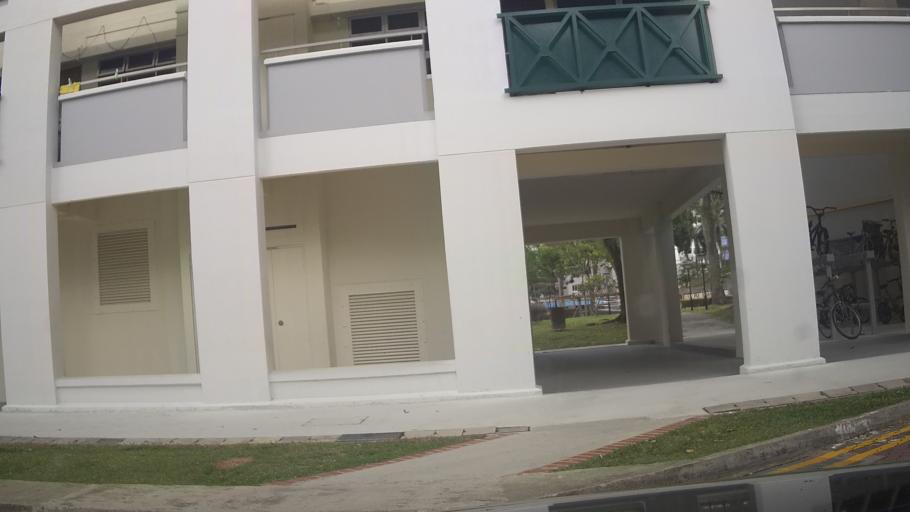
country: MY
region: Johor
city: Johor Bahru
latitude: 1.4403
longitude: 103.7898
